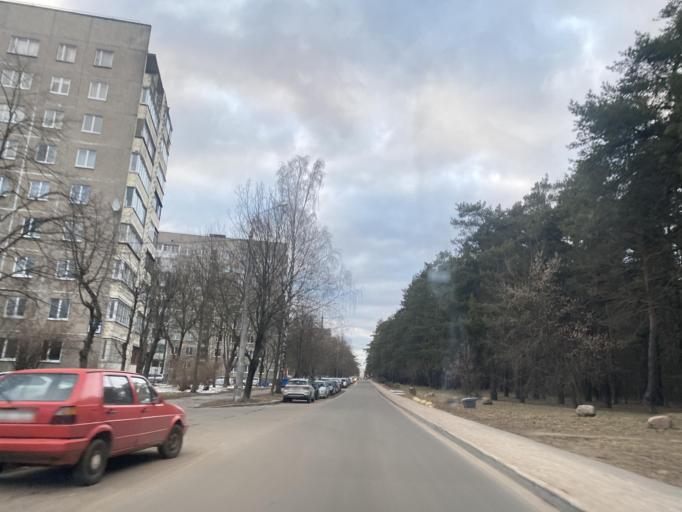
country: BY
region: Minsk
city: Borovlyany
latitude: 53.9545
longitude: 27.6366
